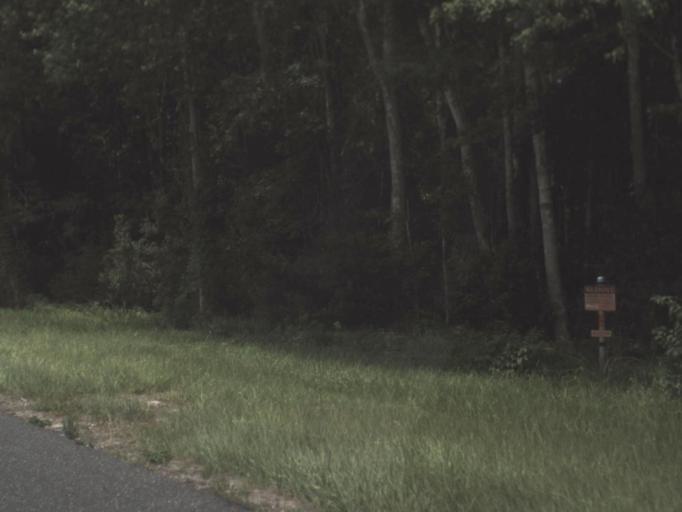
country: US
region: Florida
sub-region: Taylor County
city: Perry
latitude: 30.2499
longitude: -83.6997
